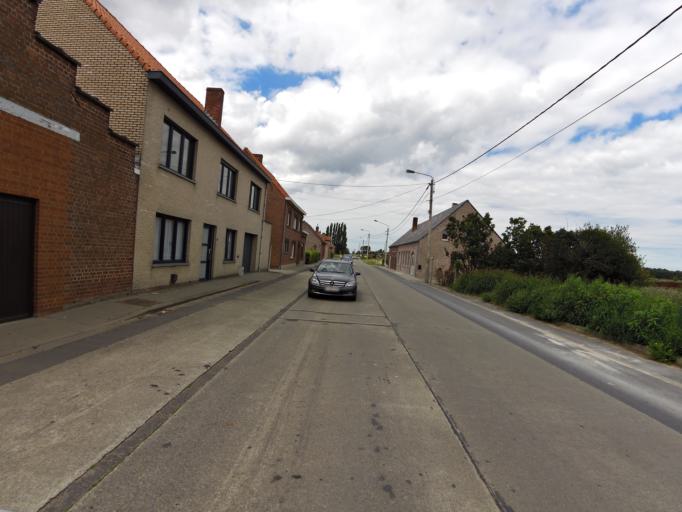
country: BE
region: Flanders
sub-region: Provincie West-Vlaanderen
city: Kortemark
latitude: 51.0533
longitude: 3.0145
